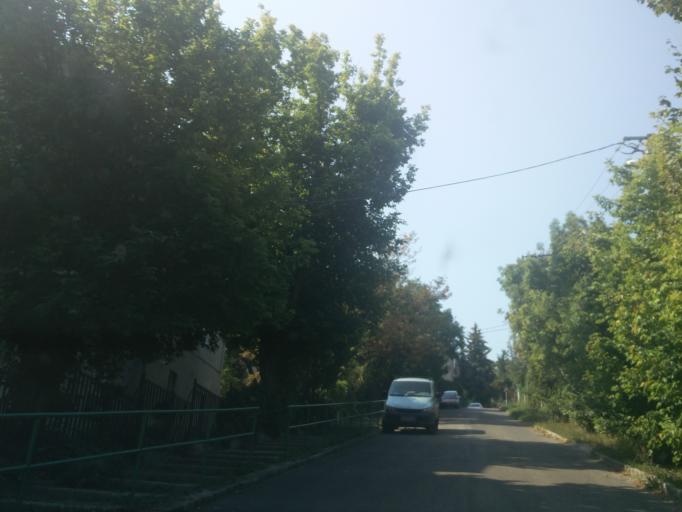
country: HU
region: Budapest
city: Budapest XII. keruelet
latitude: 47.5062
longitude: 19.0001
